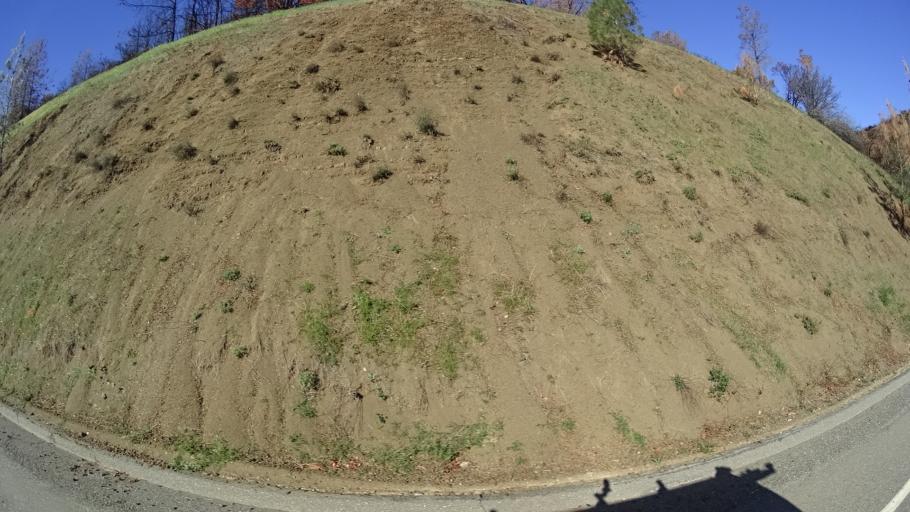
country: US
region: California
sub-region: Glenn County
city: Orland
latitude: 39.6507
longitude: -122.5939
